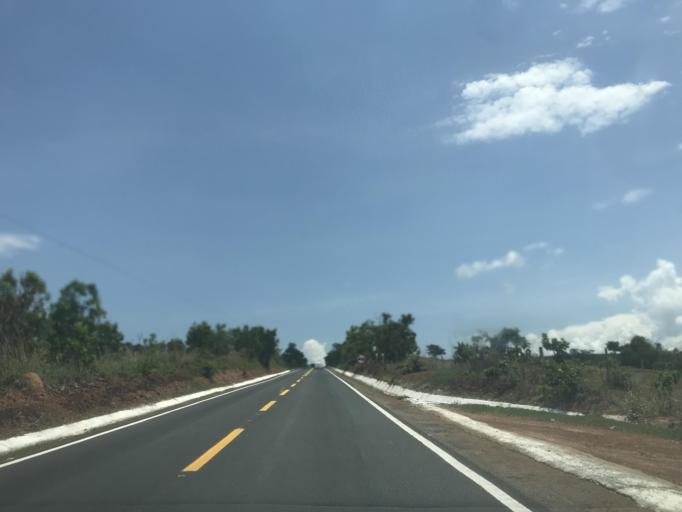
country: BR
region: Goias
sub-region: Bela Vista De Goias
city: Bela Vista de Goias
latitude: -17.1267
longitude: -48.6683
